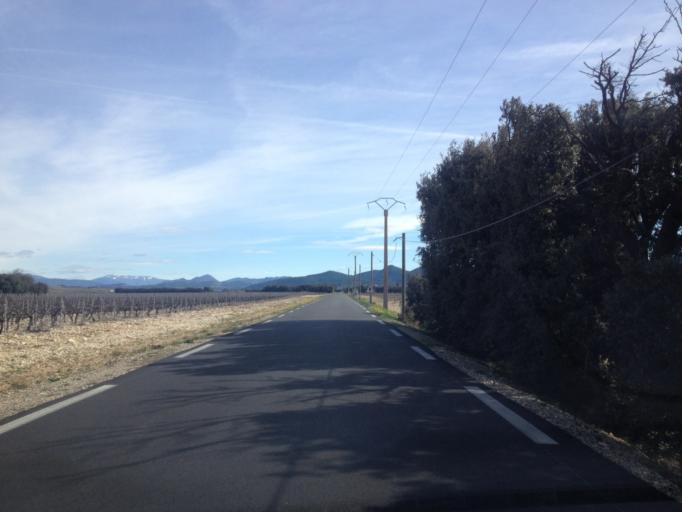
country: FR
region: Provence-Alpes-Cote d'Azur
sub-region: Departement du Vaucluse
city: Violes
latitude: 44.1867
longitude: 4.9583
